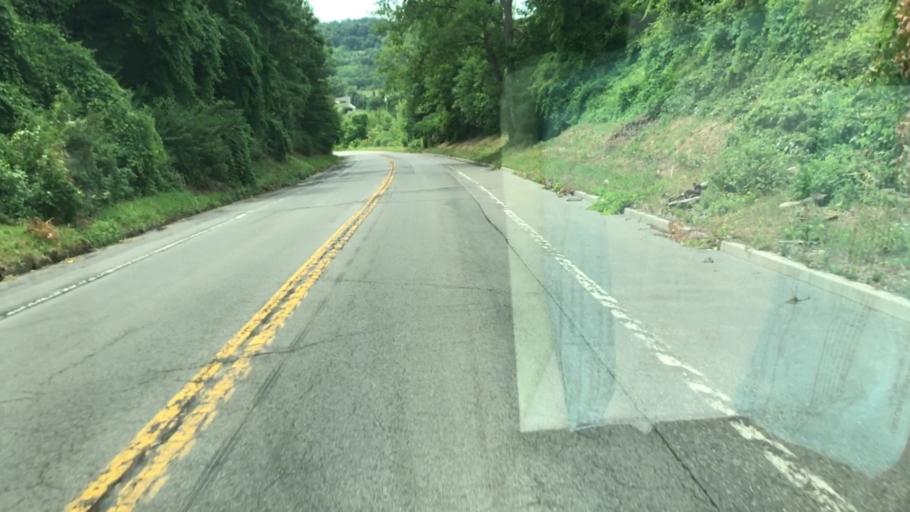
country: US
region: New York
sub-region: Onondaga County
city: Marcellus
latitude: 42.9326
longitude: -76.3222
